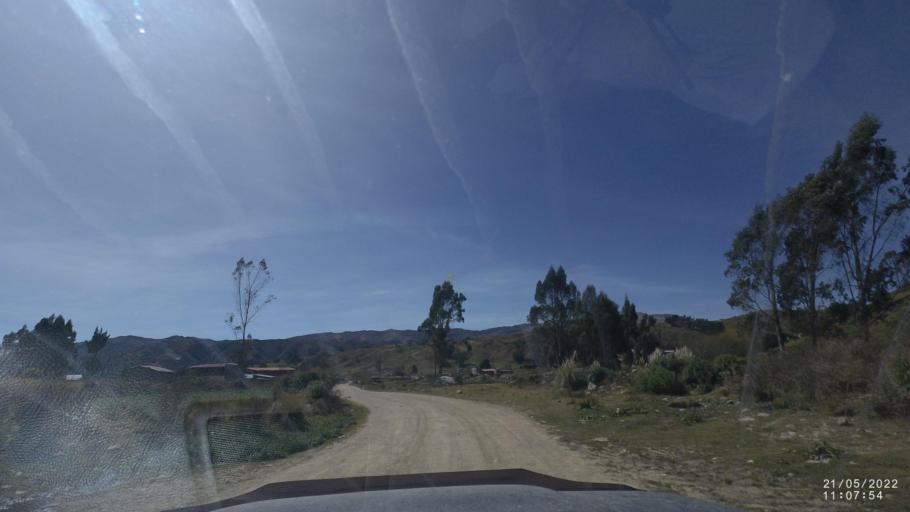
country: BO
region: Cochabamba
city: Colomi
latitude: -17.3093
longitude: -65.9148
